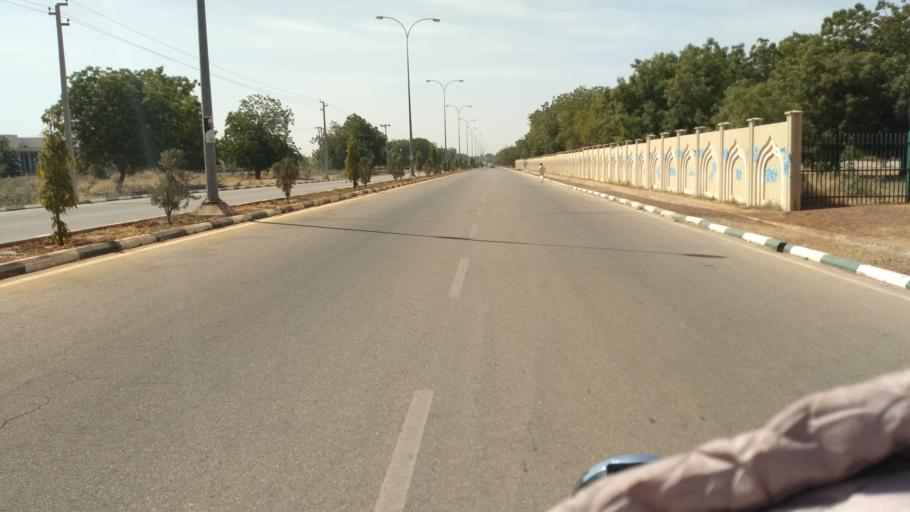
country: NG
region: Jigawa
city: Dutse
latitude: 11.6846
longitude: 9.3374
